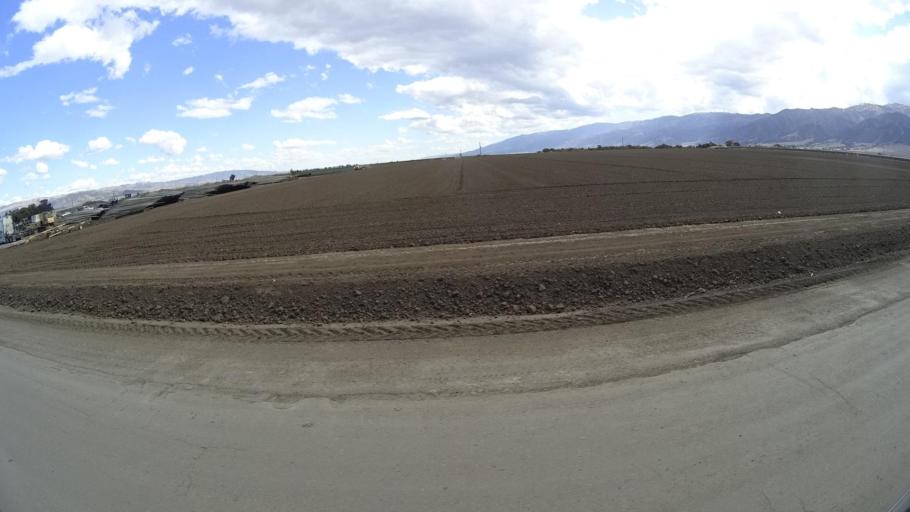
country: US
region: California
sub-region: Monterey County
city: Chualar
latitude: 36.5929
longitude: -121.5508
